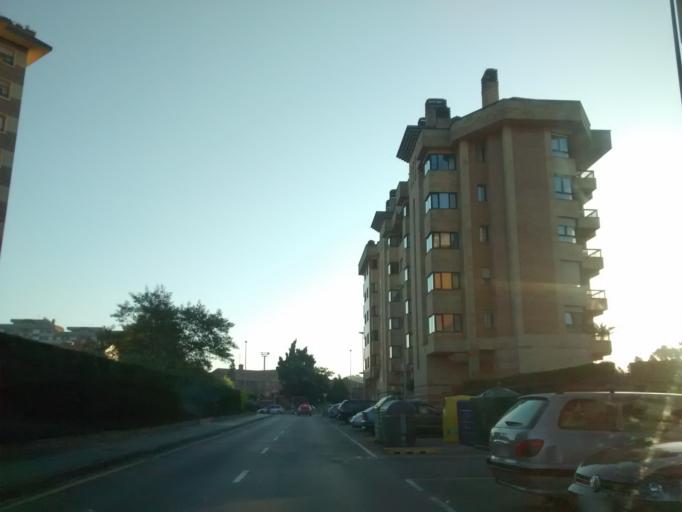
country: ES
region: Asturias
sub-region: Province of Asturias
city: Gijon
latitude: 43.5287
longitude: -5.6428
